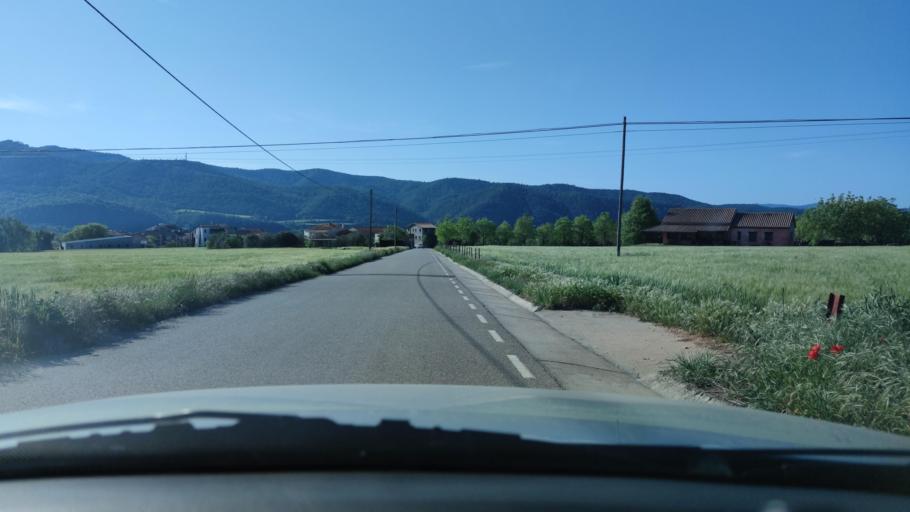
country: ES
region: Catalonia
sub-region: Provincia de Lleida
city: Oliana
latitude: 42.0631
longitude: 1.2930
